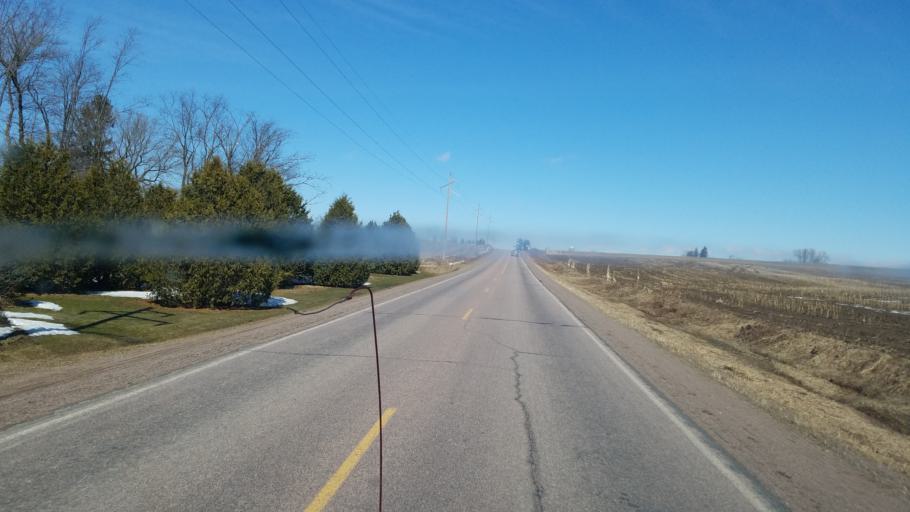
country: US
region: Wisconsin
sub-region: Clark County
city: Loyal
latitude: 44.5768
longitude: -90.3957
